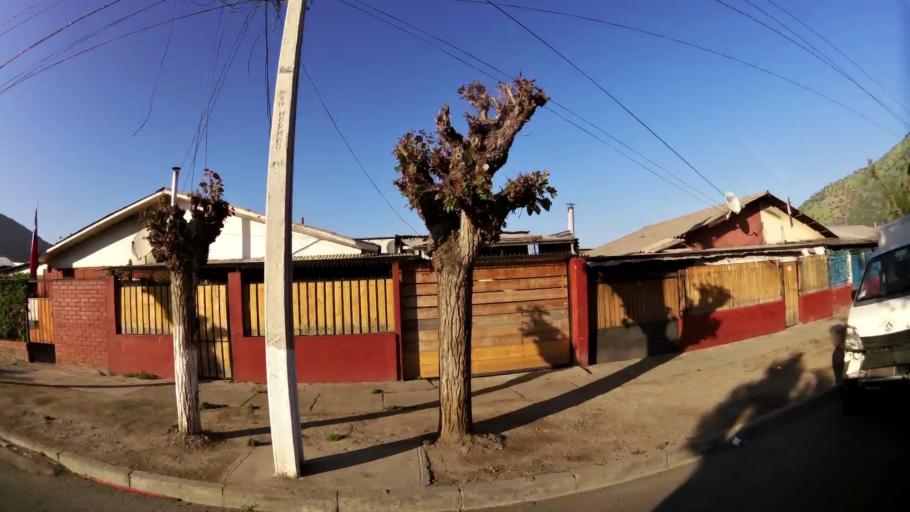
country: CL
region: Santiago Metropolitan
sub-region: Provincia de Chacabuco
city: Chicureo Abajo
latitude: -33.3613
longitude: -70.6309
